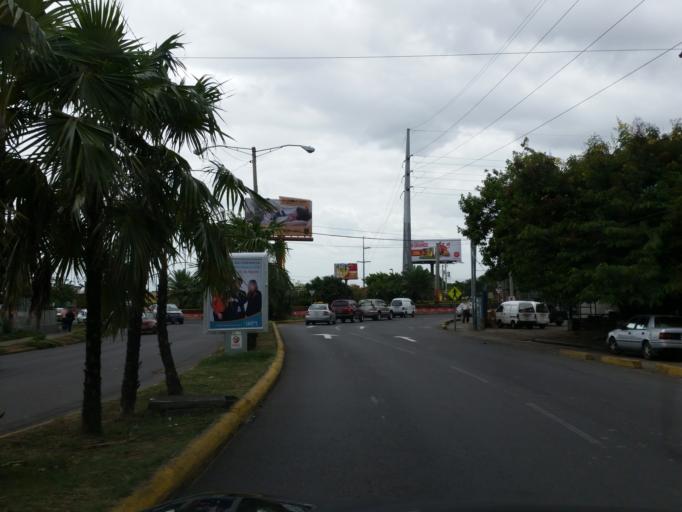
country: NI
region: Managua
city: Managua
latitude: 12.1128
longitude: -86.2562
